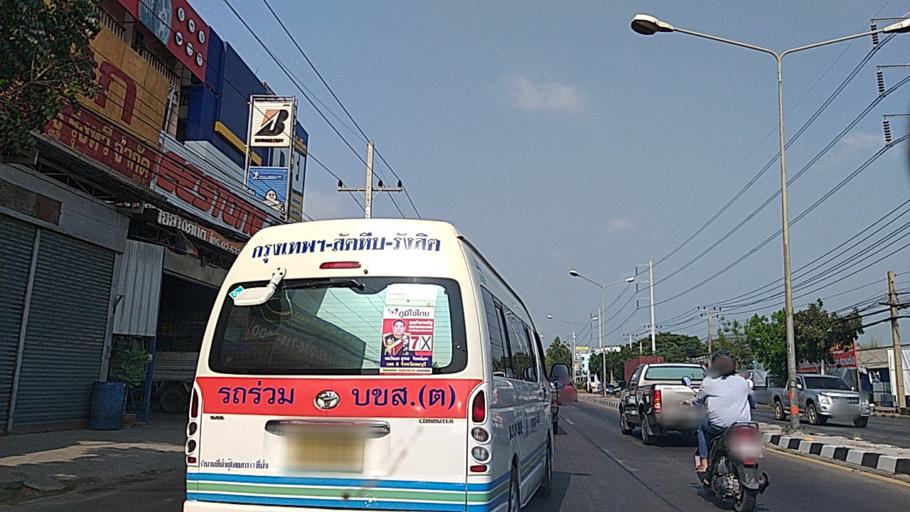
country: TH
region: Bangkok
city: Sai Mai
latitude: 13.9320
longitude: 100.6676
